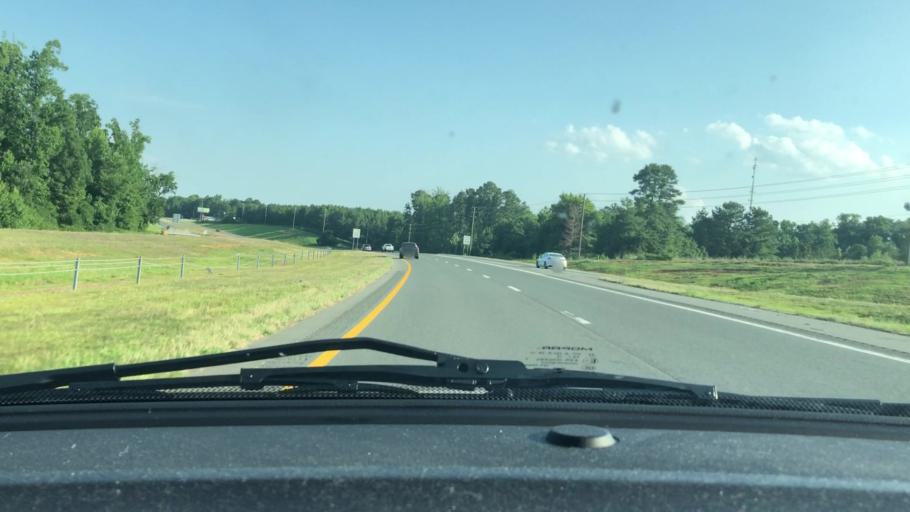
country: US
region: North Carolina
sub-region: Lee County
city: Broadway
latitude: 35.4328
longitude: -79.1229
